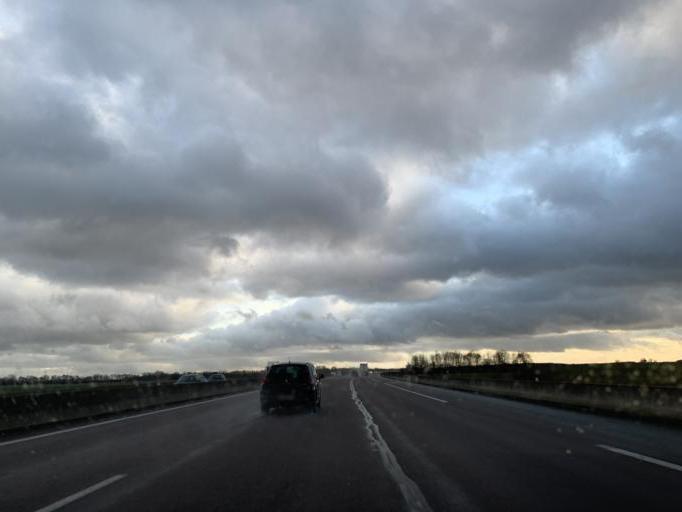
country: FR
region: Champagne-Ardenne
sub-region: Departement de la Haute-Marne
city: Langres
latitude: 47.8488
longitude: 5.2305
